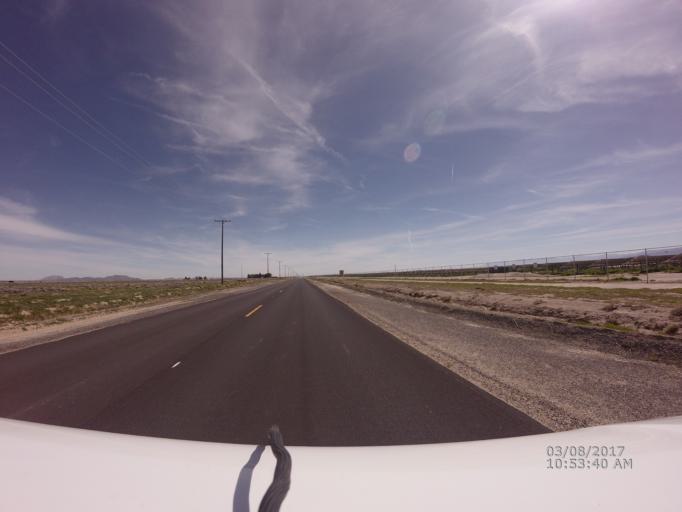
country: US
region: California
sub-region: Los Angeles County
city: Green Valley
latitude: 34.8192
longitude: -118.3890
